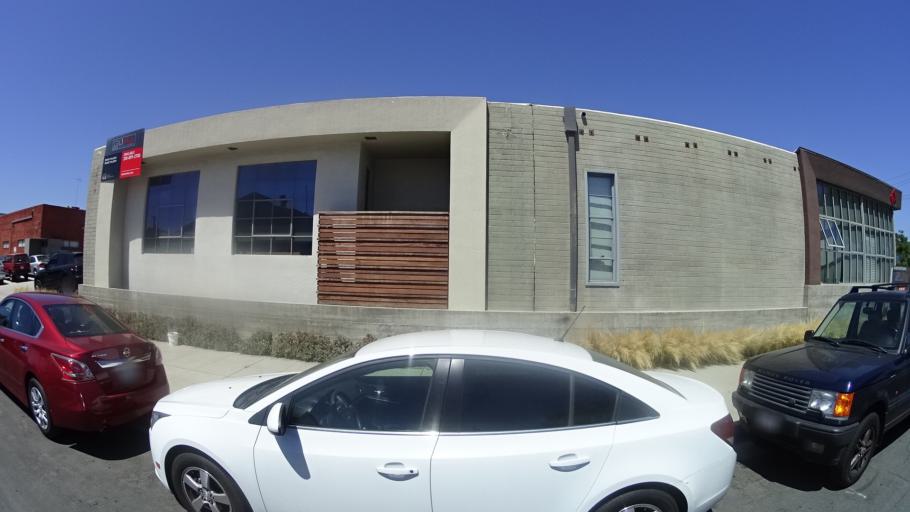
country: US
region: California
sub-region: Los Angeles County
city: Santa Monica
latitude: 34.0237
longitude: -118.4764
